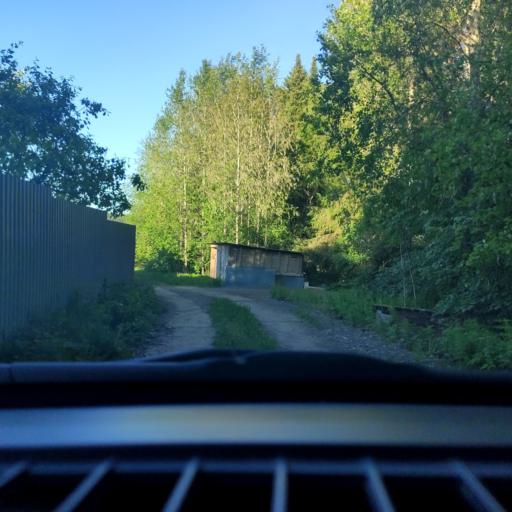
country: RU
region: Perm
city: Ferma
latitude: 57.9675
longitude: 56.3884
